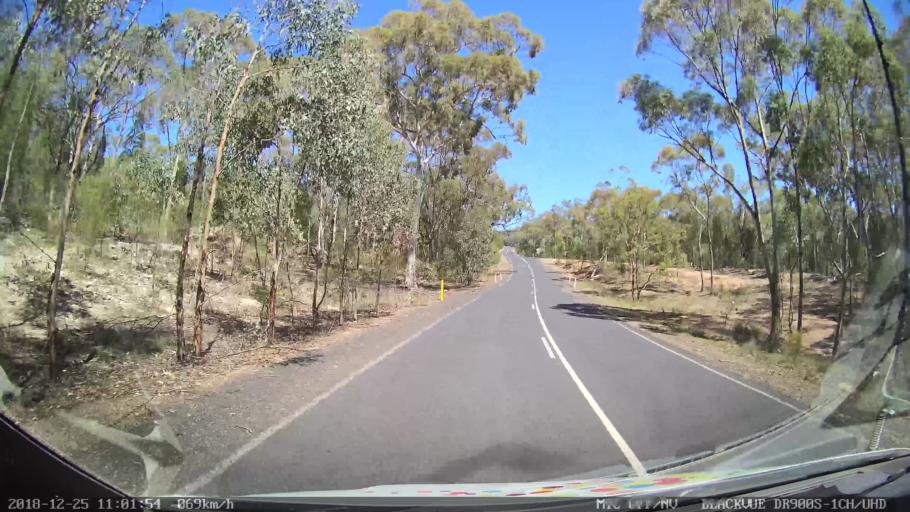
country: AU
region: New South Wales
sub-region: Upper Hunter Shire
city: Merriwa
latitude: -32.4061
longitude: 150.1962
